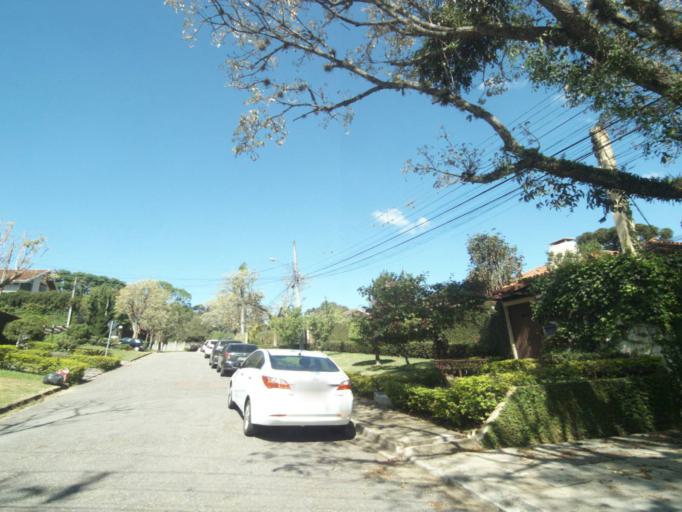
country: BR
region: Parana
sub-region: Curitiba
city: Curitiba
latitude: -25.4008
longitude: -49.2697
